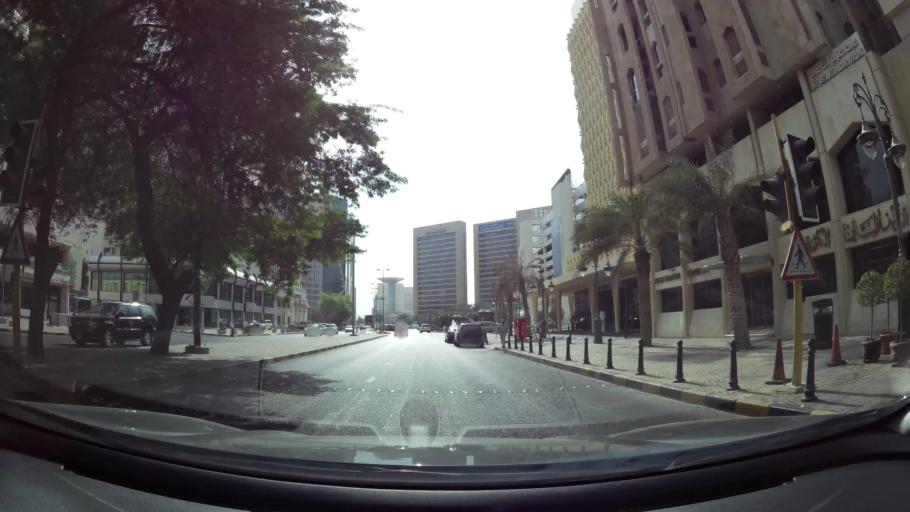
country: KW
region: Al Asimah
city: Kuwait City
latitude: 29.3771
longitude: 47.9757
